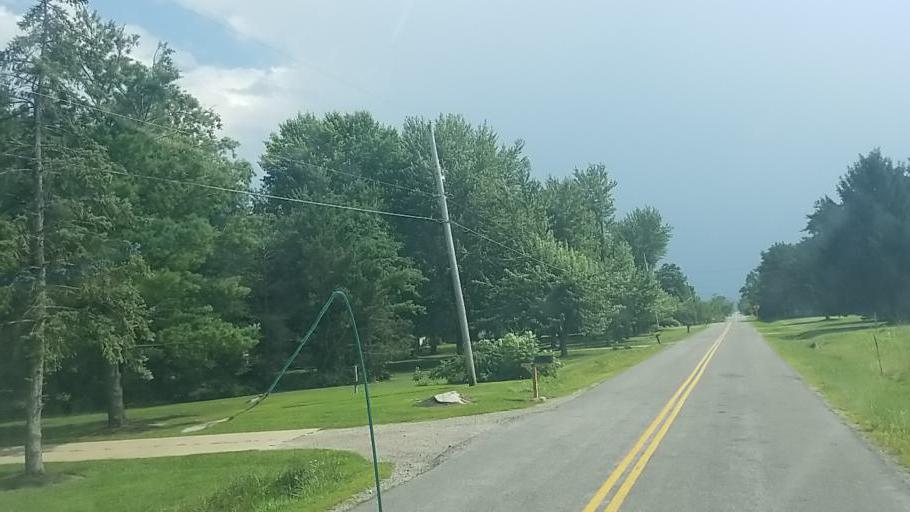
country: US
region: Ohio
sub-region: Medina County
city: Westfield Center
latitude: 41.1041
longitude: -81.9622
